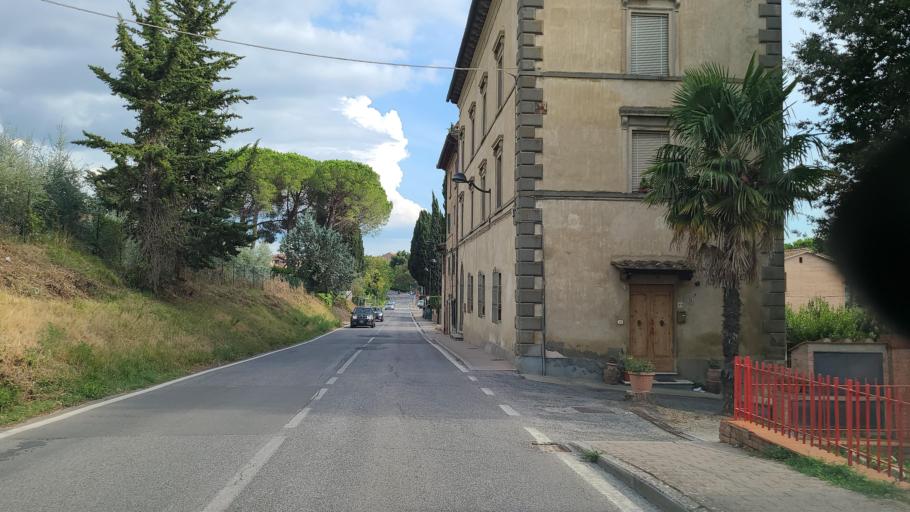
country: IT
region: Tuscany
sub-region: Provincia di Siena
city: San Gimignano
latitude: 43.4741
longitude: 11.0312
